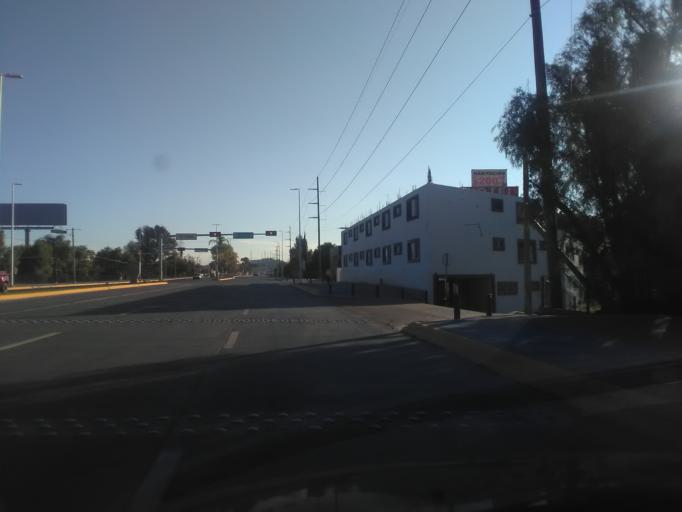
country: MX
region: Durango
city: Victoria de Durango
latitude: 23.9945
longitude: -104.7041
